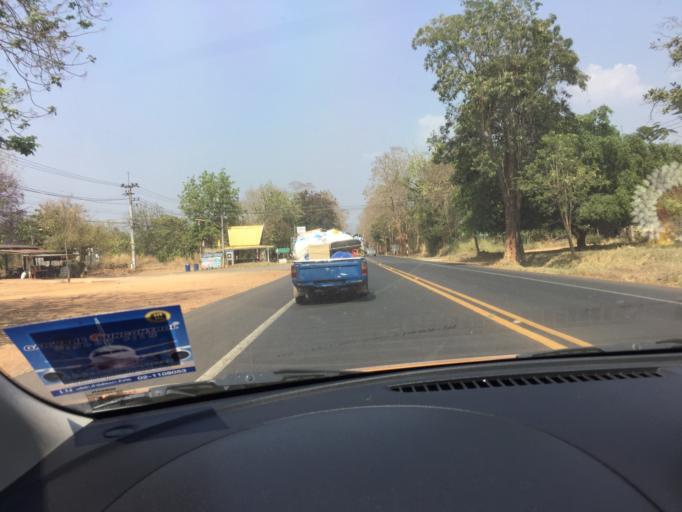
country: TH
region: Kanchanaburi
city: Sai Yok
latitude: 14.1749
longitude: 99.1286
